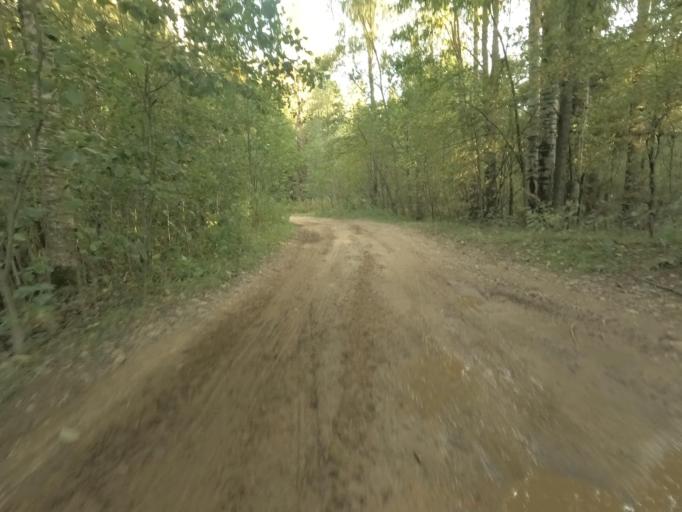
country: RU
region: Leningrad
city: Otradnoye
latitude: 59.8537
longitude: 30.7949
